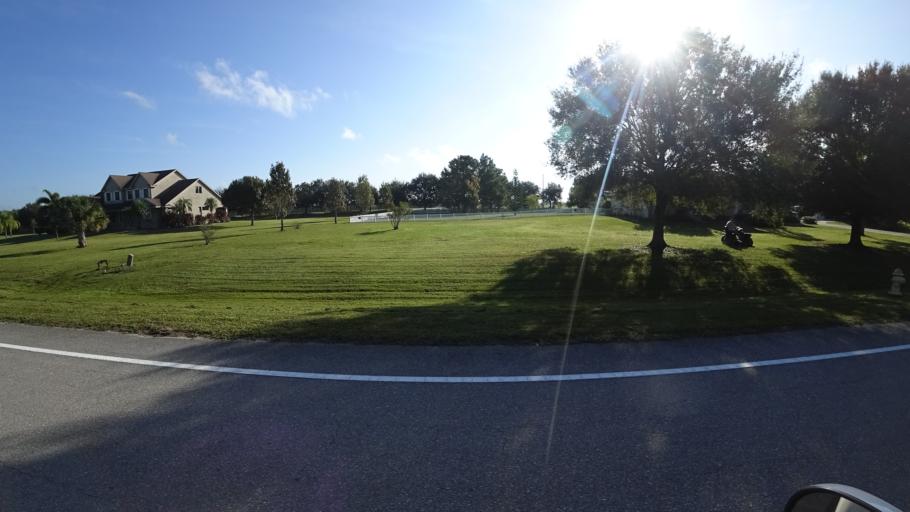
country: US
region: Florida
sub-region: Hillsborough County
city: Sun City Center
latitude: 27.5506
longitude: -82.3528
